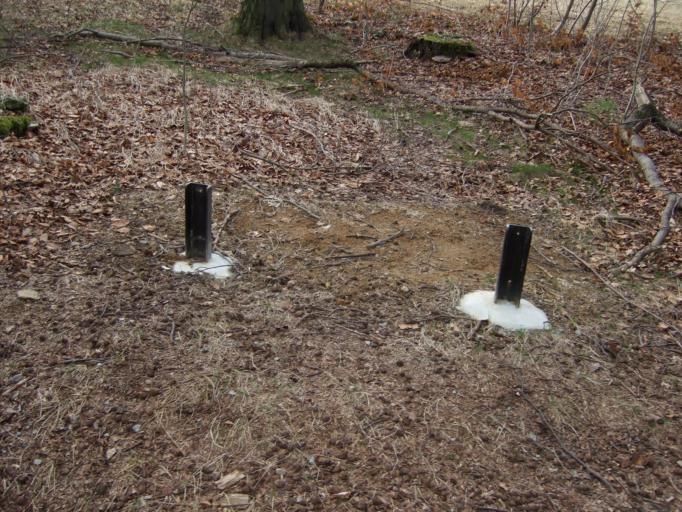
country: DE
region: Saxony
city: Brand-Erbisdorf
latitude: 50.8551
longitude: 13.3386
